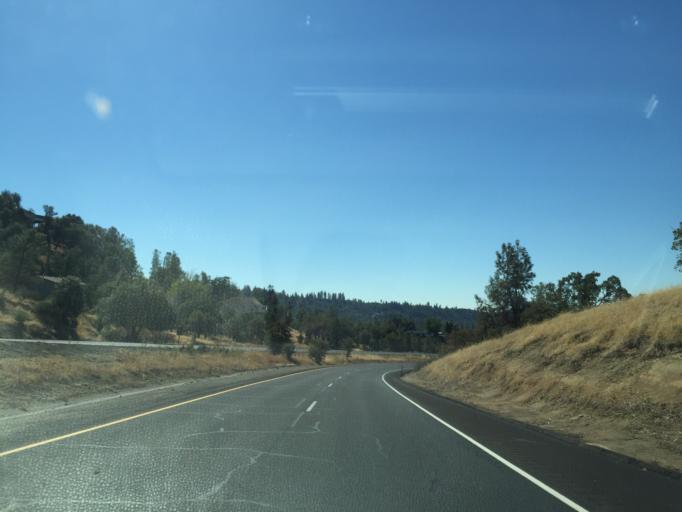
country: US
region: California
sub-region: Tuolumne County
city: Mono Vista
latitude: 38.0039
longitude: -120.2601
